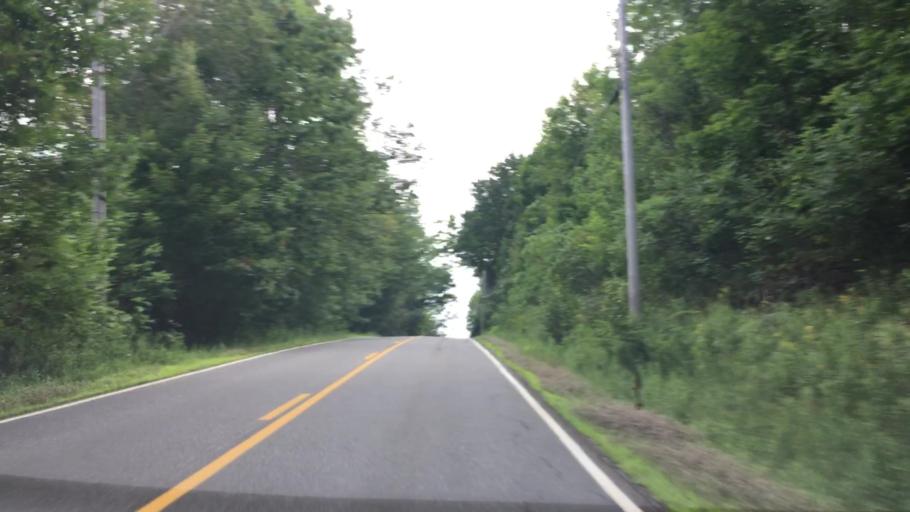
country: US
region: Maine
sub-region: Waldo County
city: Belfast
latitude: 44.3607
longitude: -69.0459
